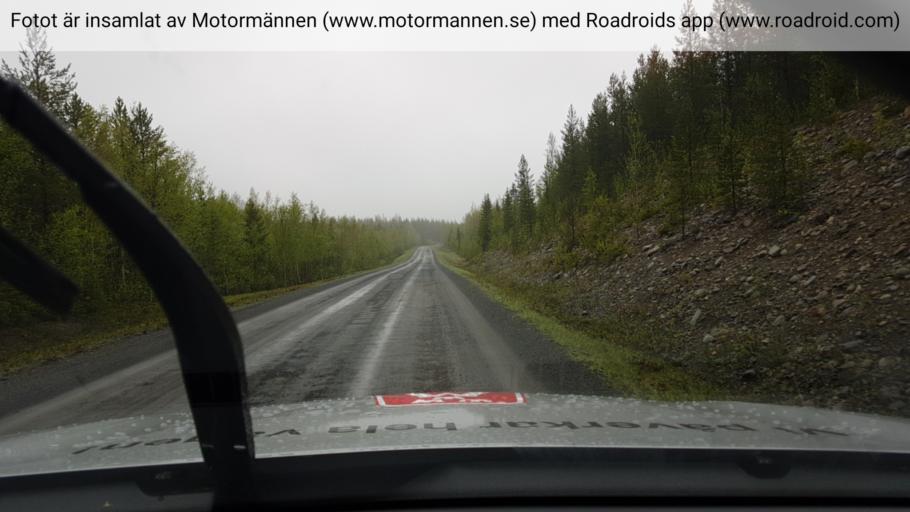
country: SE
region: Jaemtland
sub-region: Krokoms Kommun
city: Valla
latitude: 63.0679
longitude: 13.9589
